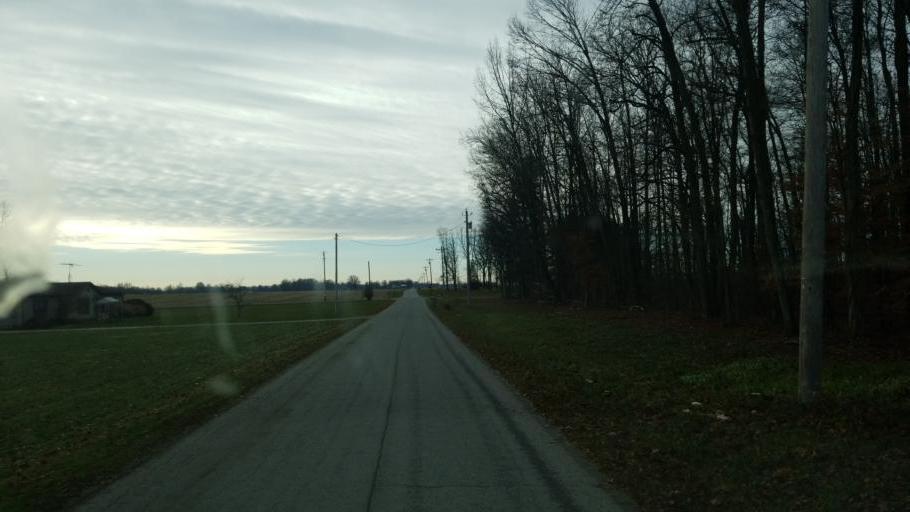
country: US
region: Ohio
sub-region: Morrow County
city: Cardington
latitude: 40.6175
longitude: -82.9526
